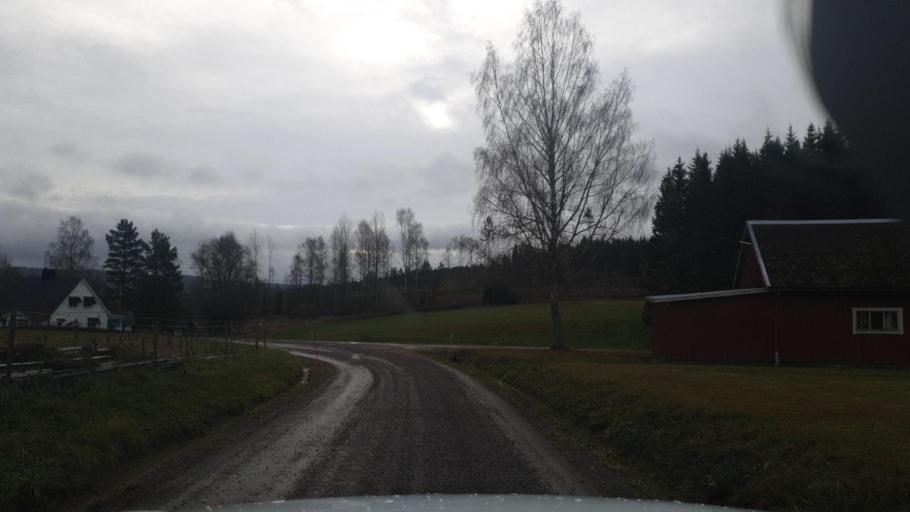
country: NO
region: Ostfold
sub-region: Romskog
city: Romskog
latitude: 59.8125
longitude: 11.9964
